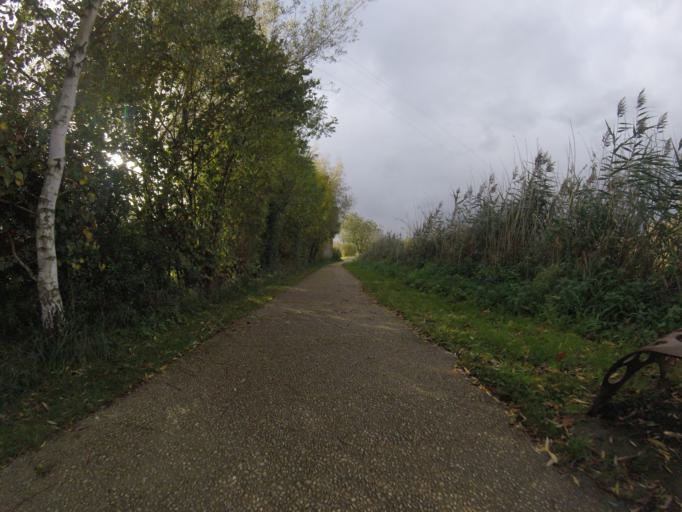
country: FR
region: Nord-Pas-de-Calais
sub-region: Departement du Pas-de-Calais
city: Sailly-sur-la-Lys
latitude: 50.6644
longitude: 2.7807
